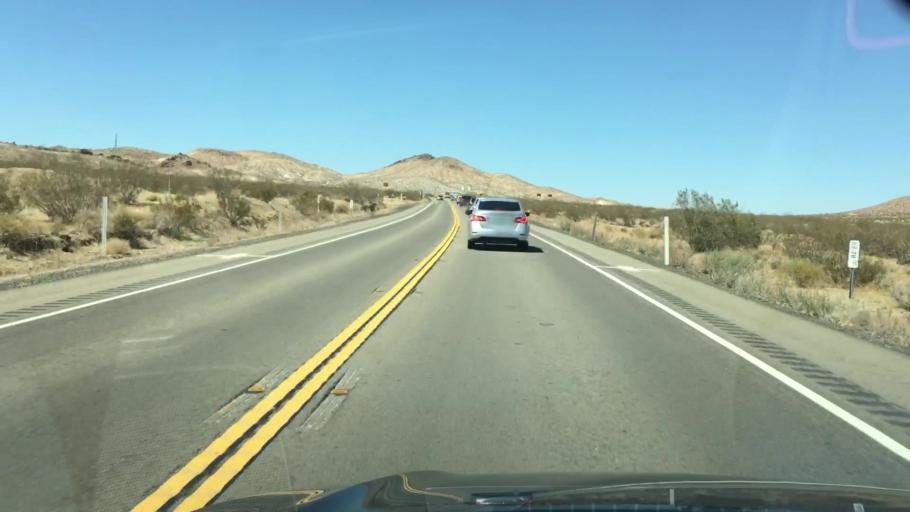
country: US
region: California
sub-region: Kern County
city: Ridgecrest
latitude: 35.3363
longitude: -117.6189
